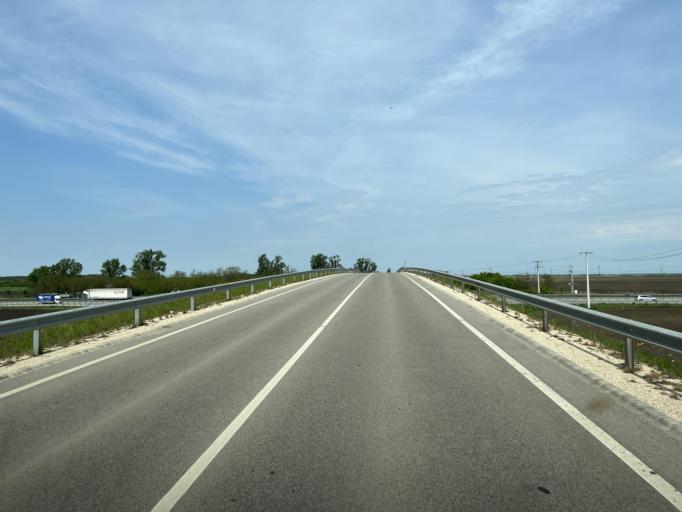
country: HU
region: Pest
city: Abony
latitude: 47.2155
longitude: 19.9805
